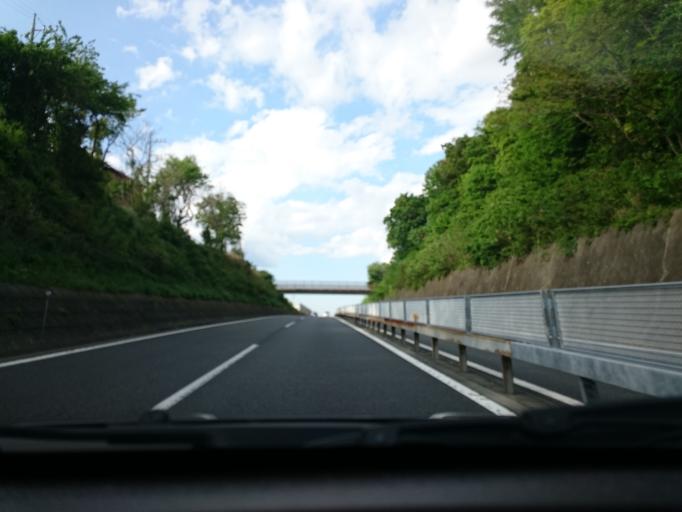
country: JP
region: Kanagawa
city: Isehara
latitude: 35.3518
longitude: 139.2987
